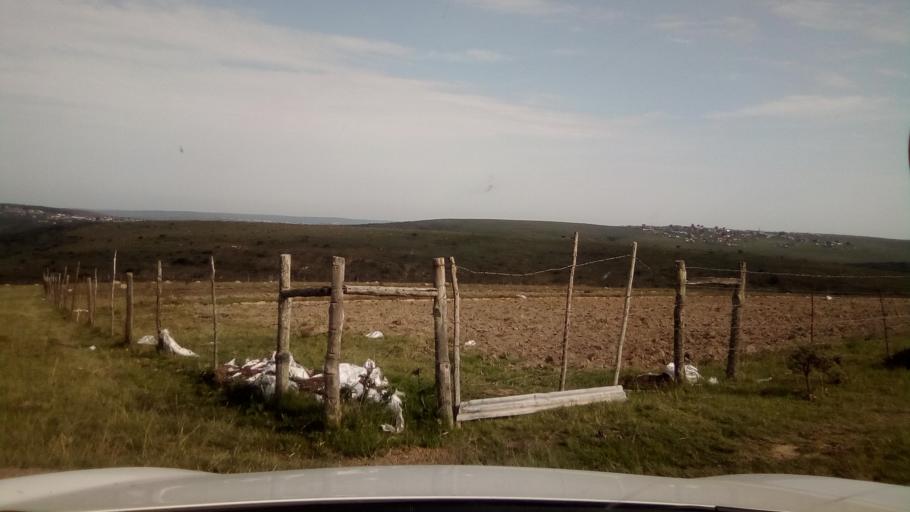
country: ZA
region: Eastern Cape
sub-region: Buffalo City Metropolitan Municipality
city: Bhisho
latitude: -33.0080
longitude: 27.3005
